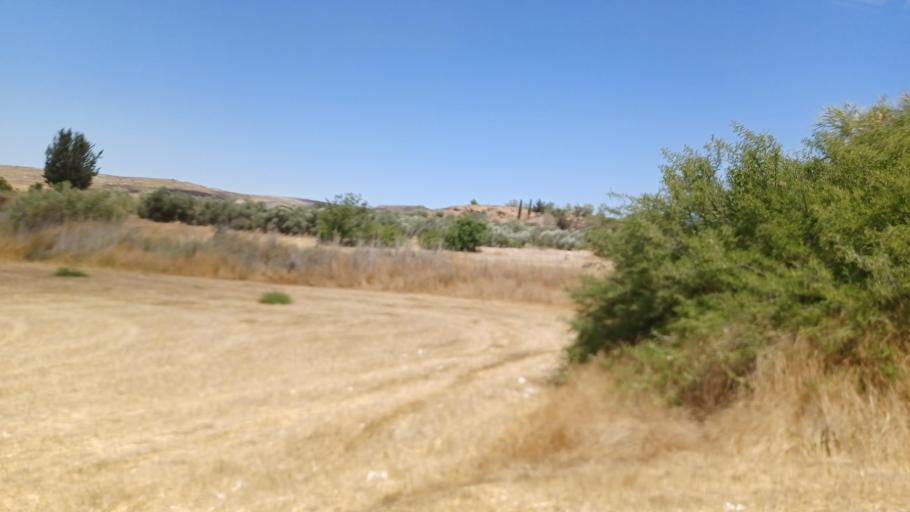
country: CY
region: Larnaka
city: Troulloi
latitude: 35.0392
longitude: 33.6173
